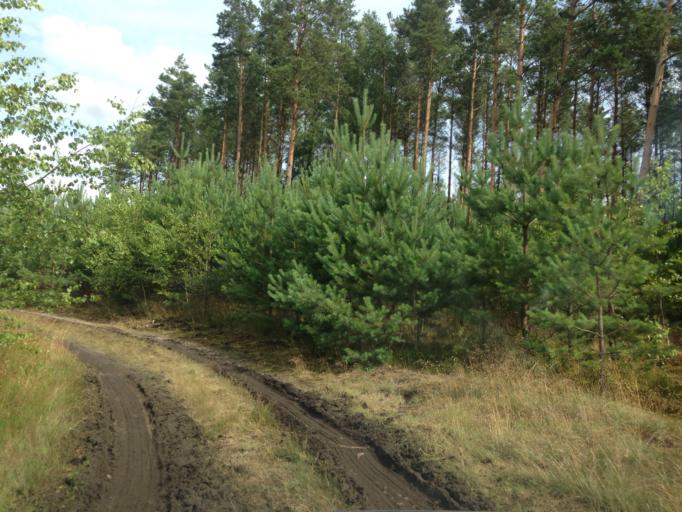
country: PL
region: Pomeranian Voivodeship
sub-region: Powiat bytowski
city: Studzienice
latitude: 54.0627
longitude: 17.6681
